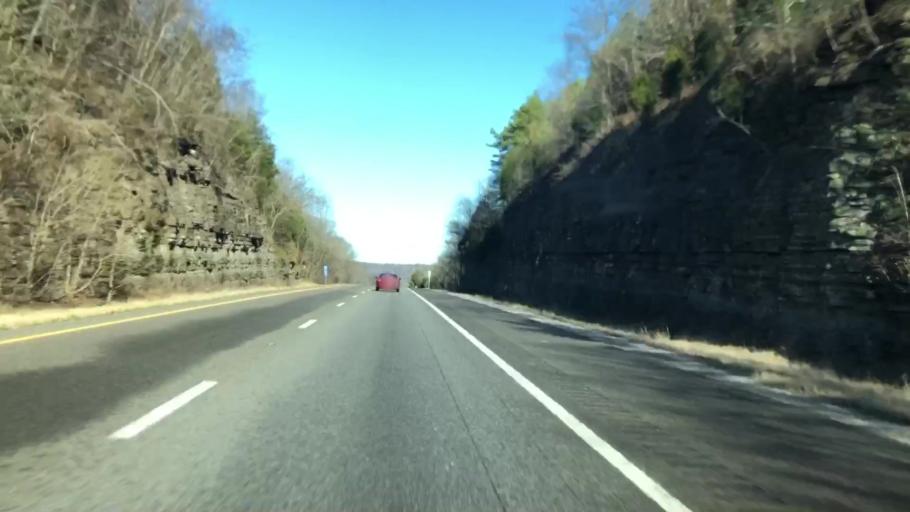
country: US
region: Tennessee
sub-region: Marshall County
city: Cornersville
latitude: 35.3556
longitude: -86.8843
